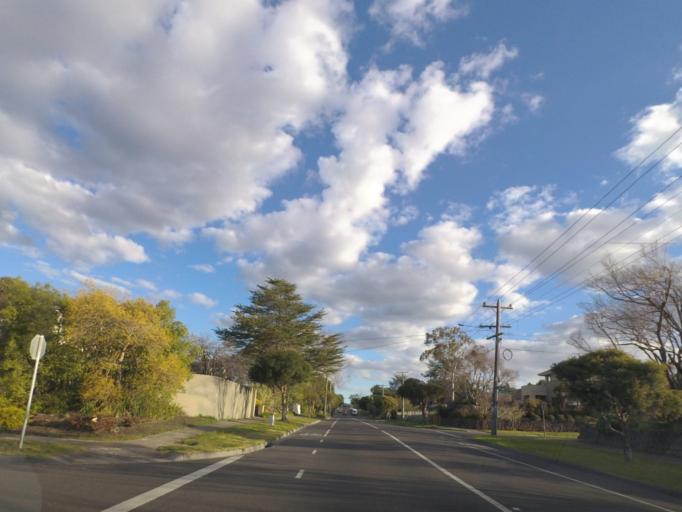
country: AU
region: Victoria
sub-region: Boroondara
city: Balwyn North
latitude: -37.7938
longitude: 145.0991
